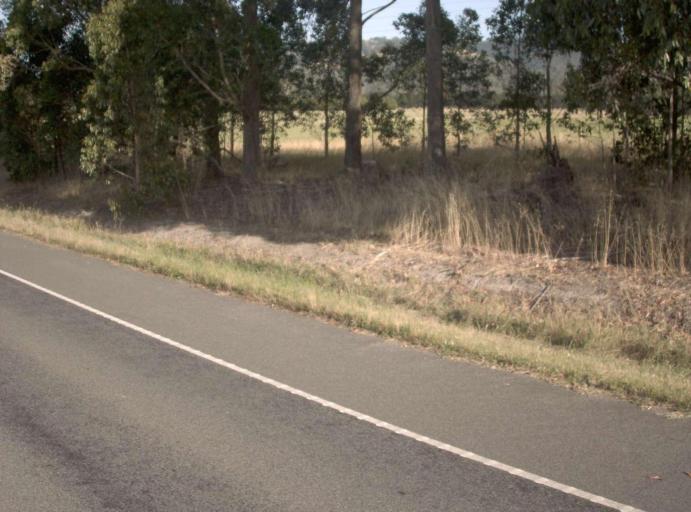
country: AU
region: Victoria
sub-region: Latrobe
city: Morwell
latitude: -38.3341
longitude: 146.3885
